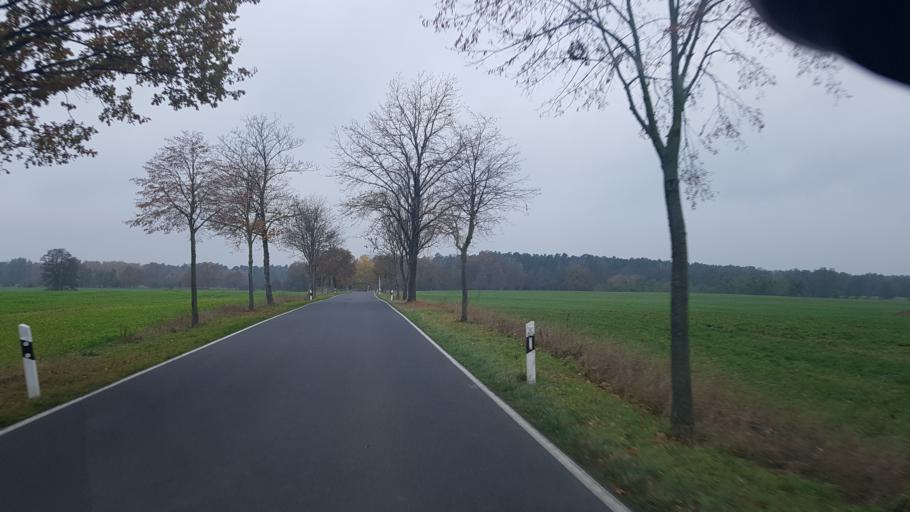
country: DE
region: Brandenburg
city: Schonermark
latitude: 52.9306
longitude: 13.0807
